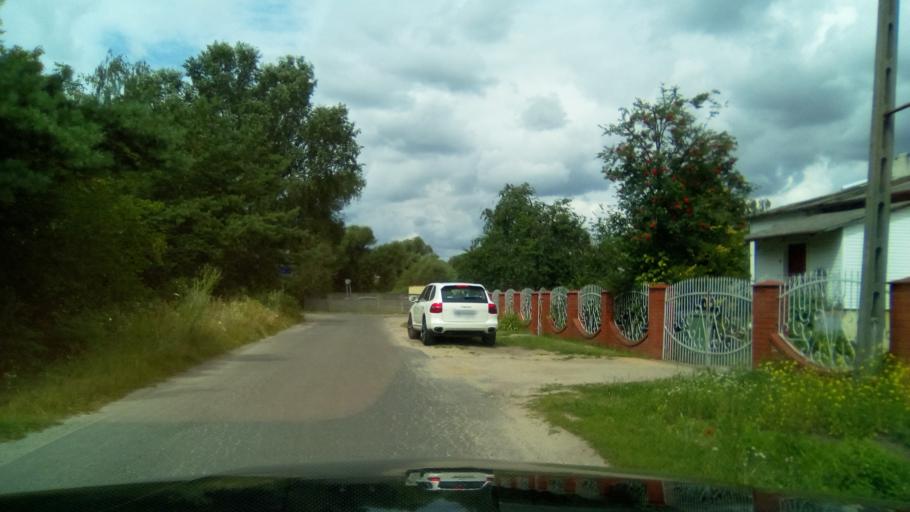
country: PL
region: Greater Poland Voivodeship
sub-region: Powiat gnieznienski
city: Gniezno
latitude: 52.5145
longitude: 17.6238
